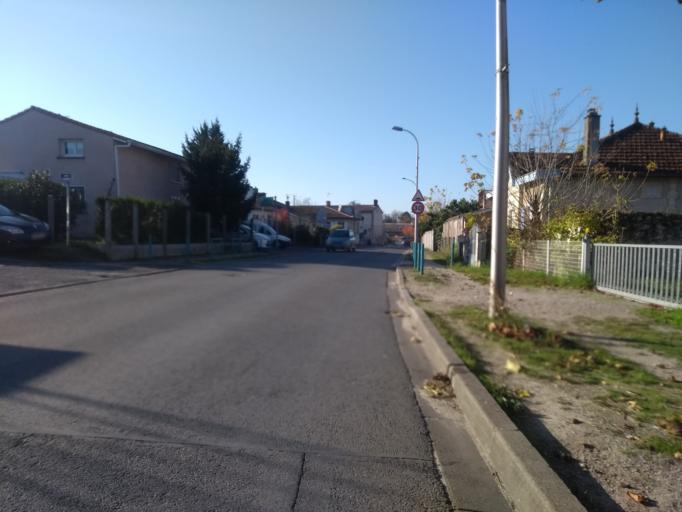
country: FR
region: Aquitaine
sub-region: Departement de la Gironde
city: Ayguemorte-les-Graves
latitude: 44.7175
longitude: -0.5073
